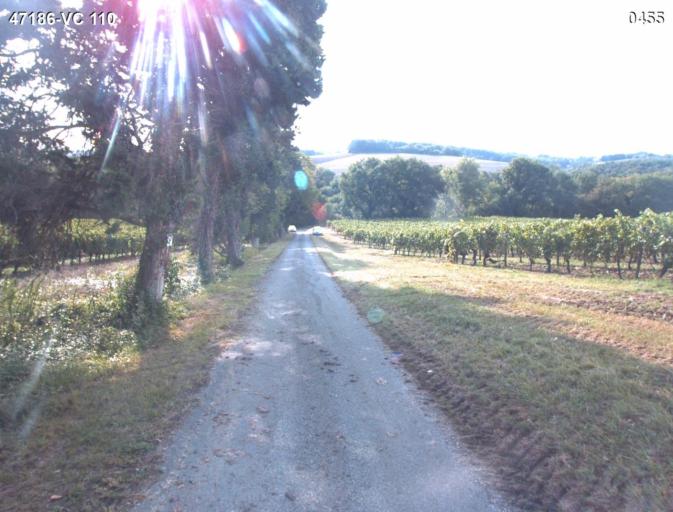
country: FR
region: Aquitaine
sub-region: Departement du Lot-et-Garonne
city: Sainte-Colombe-en-Bruilhois
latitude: 44.1881
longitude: 0.4385
